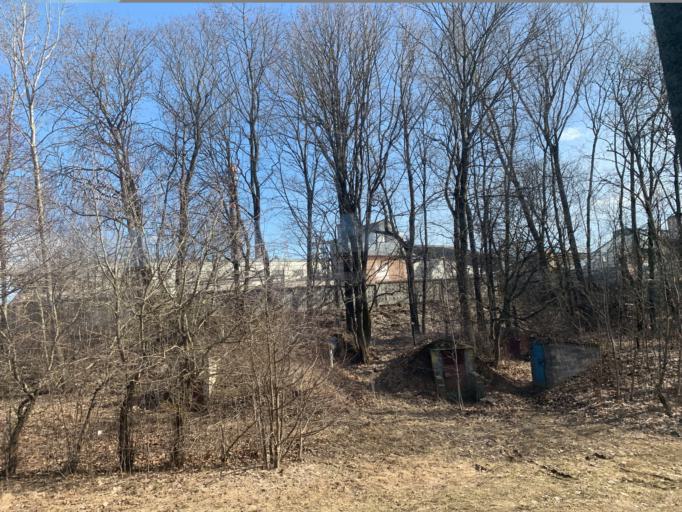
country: BY
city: Fanipol
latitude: 53.7398
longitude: 27.3241
